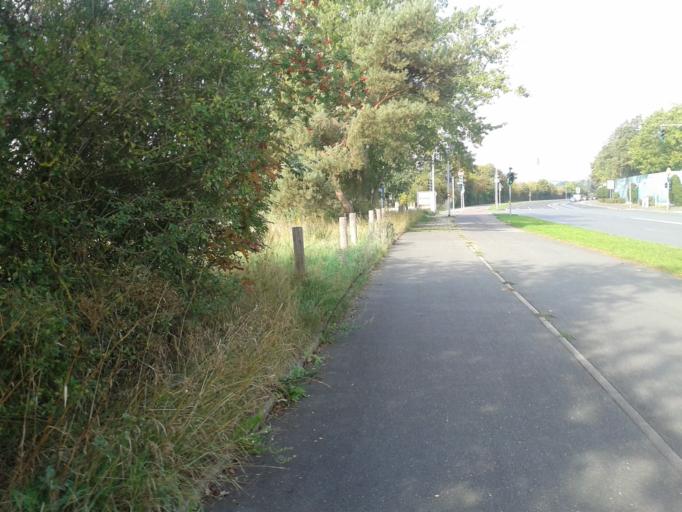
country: DE
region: Bavaria
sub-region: Upper Franconia
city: Bamberg
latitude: 49.8802
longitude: 10.9193
